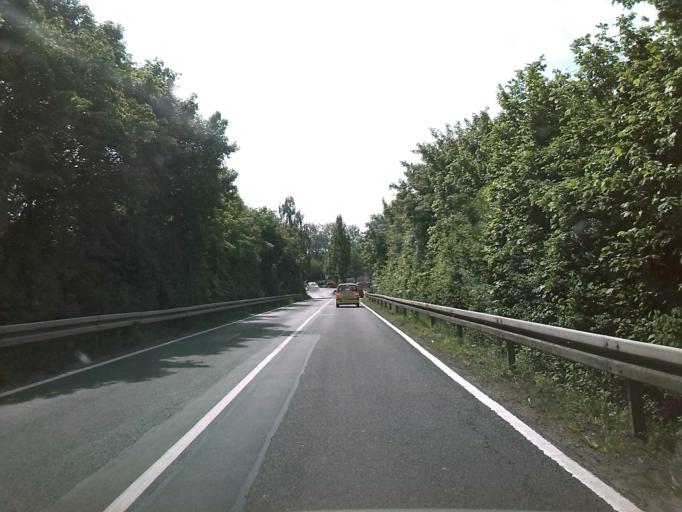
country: DE
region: Hesse
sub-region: Regierungsbezirk Darmstadt
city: Gross-Zimmern
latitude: 49.8831
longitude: 8.8148
